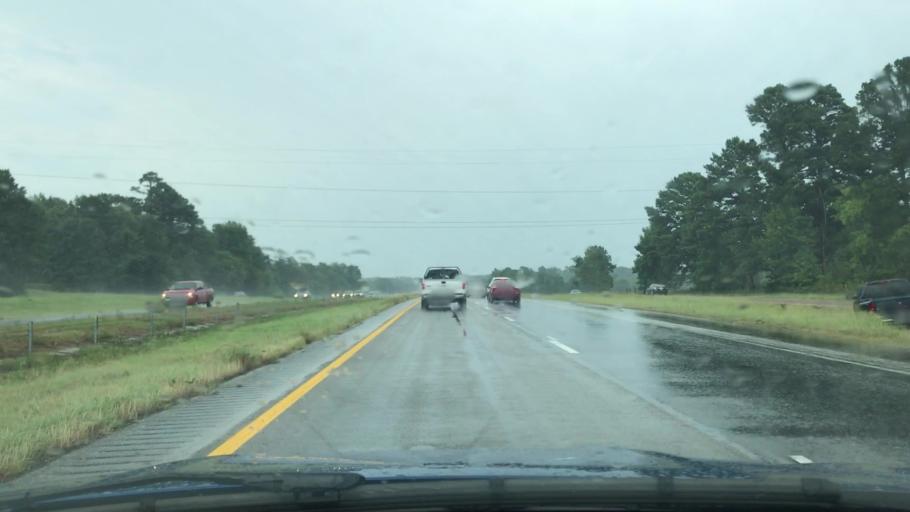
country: US
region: Texas
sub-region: Harrison County
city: Waskom
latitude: 32.4901
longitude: -94.1460
